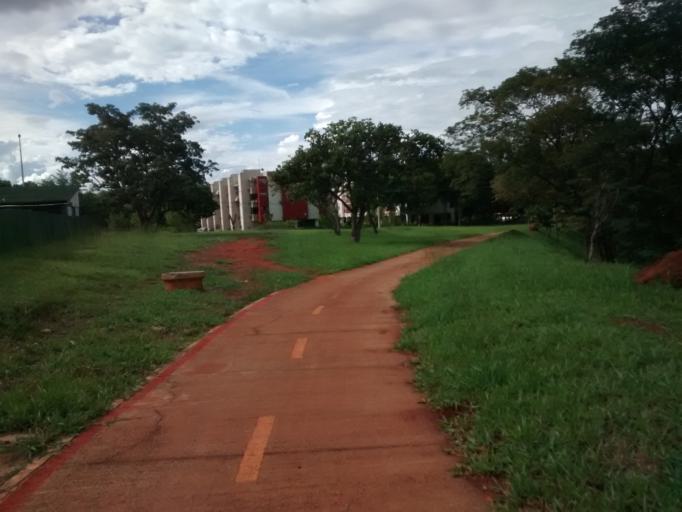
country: BR
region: Federal District
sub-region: Brasilia
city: Brasilia
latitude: -15.7847
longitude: -47.8749
